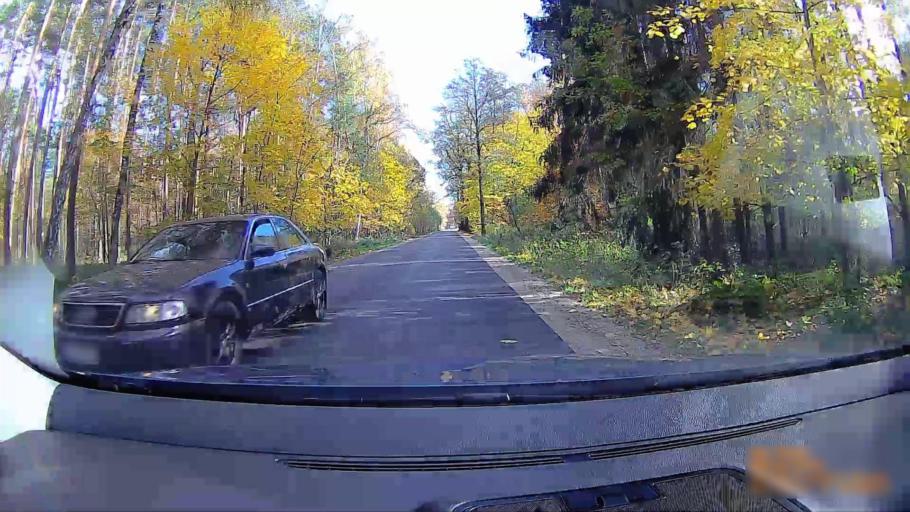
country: PL
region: Greater Poland Voivodeship
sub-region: Powiat ostrzeszowski
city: Doruchow
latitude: 51.4058
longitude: 18.0097
